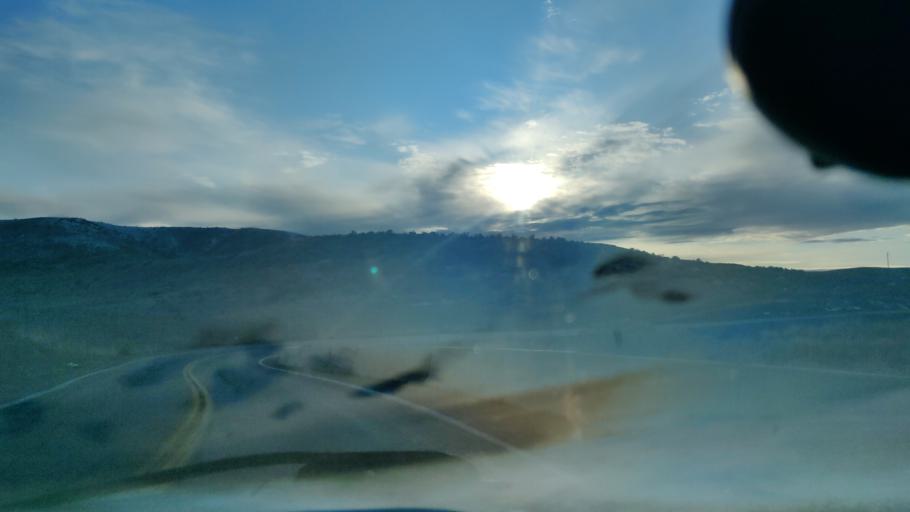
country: US
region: Idaho
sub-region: Ada County
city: Eagle
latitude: 43.7297
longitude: -116.2790
